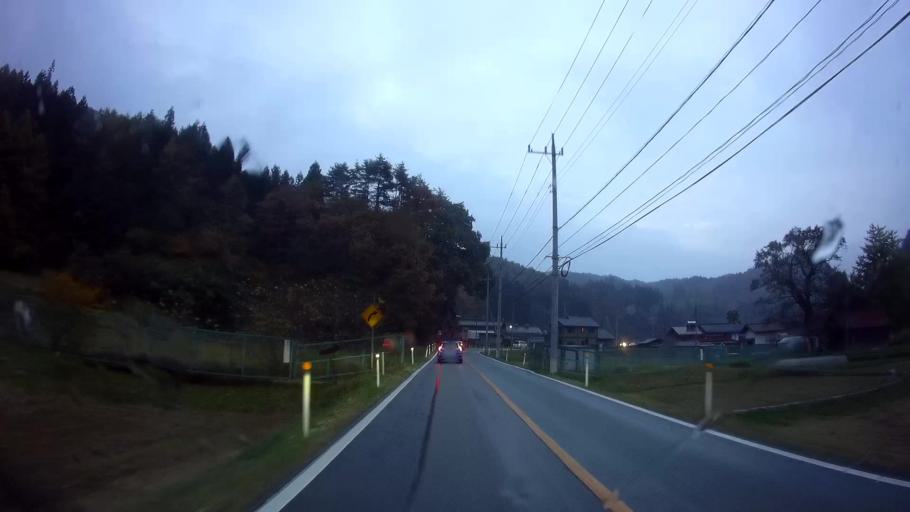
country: JP
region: Gunma
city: Nakanojomachi
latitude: 36.5252
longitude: 138.7821
